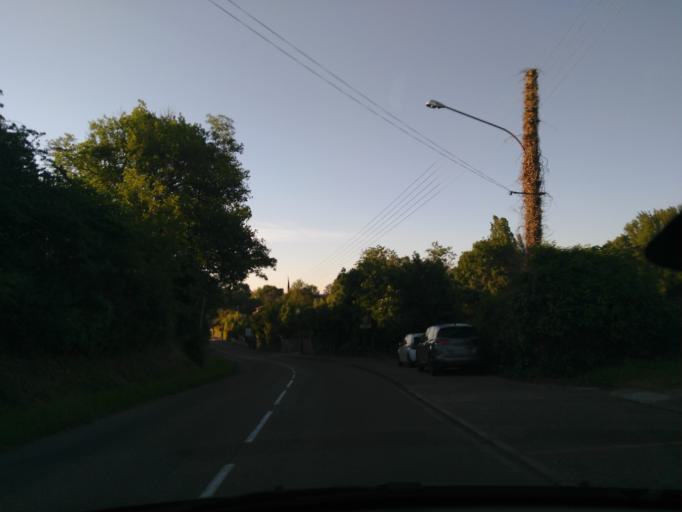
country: FR
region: Midi-Pyrenees
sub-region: Departement de la Haute-Garonne
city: Aussonne
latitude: 43.6819
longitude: 1.3209
